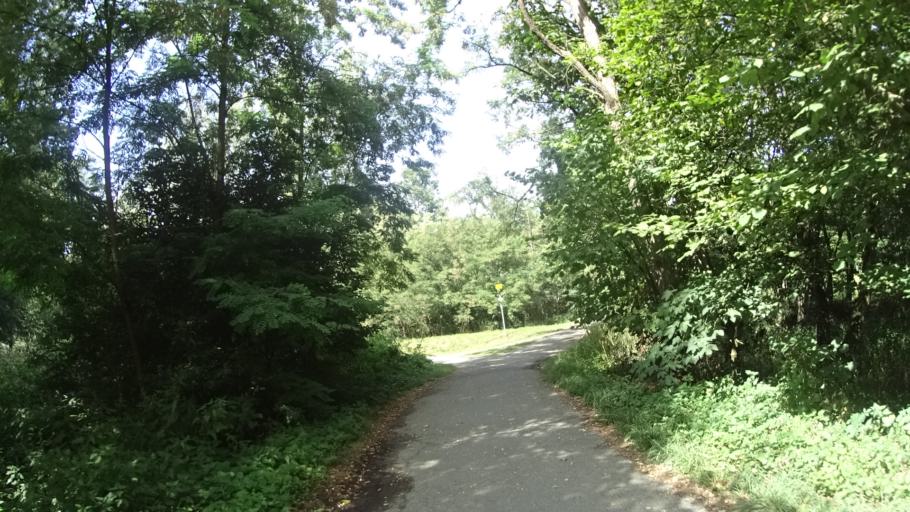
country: CZ
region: Olomoucky
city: Skrben
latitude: 49.6731
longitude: 17.1727
